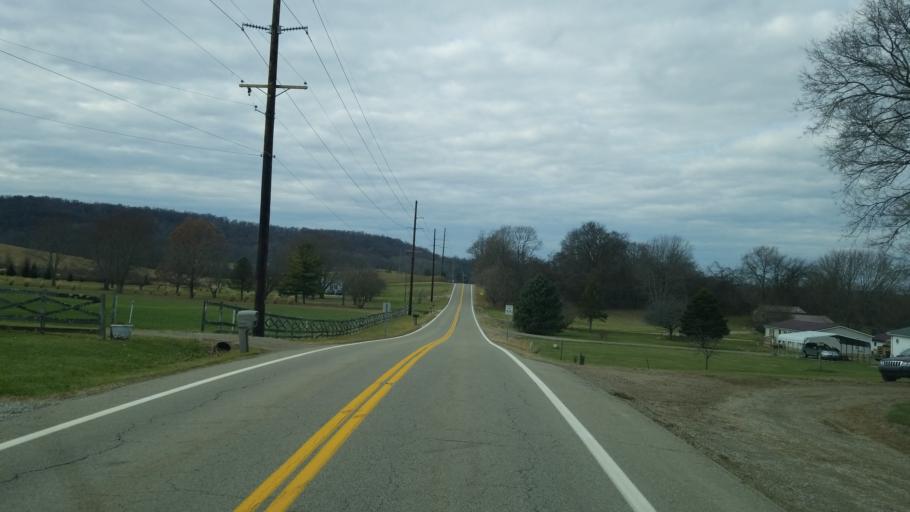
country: US
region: Ohio
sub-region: Ross County
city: Frankfort
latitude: 39.3483
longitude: -83.2091
